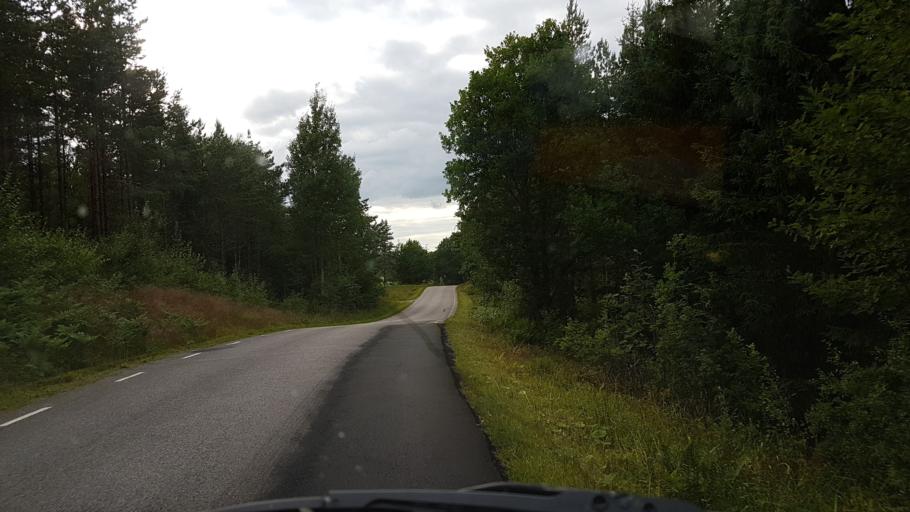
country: SE
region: OEstergoetland
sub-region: Valdemarsviks Kommun
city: Gusum
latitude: 58.4566
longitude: 16.5915
